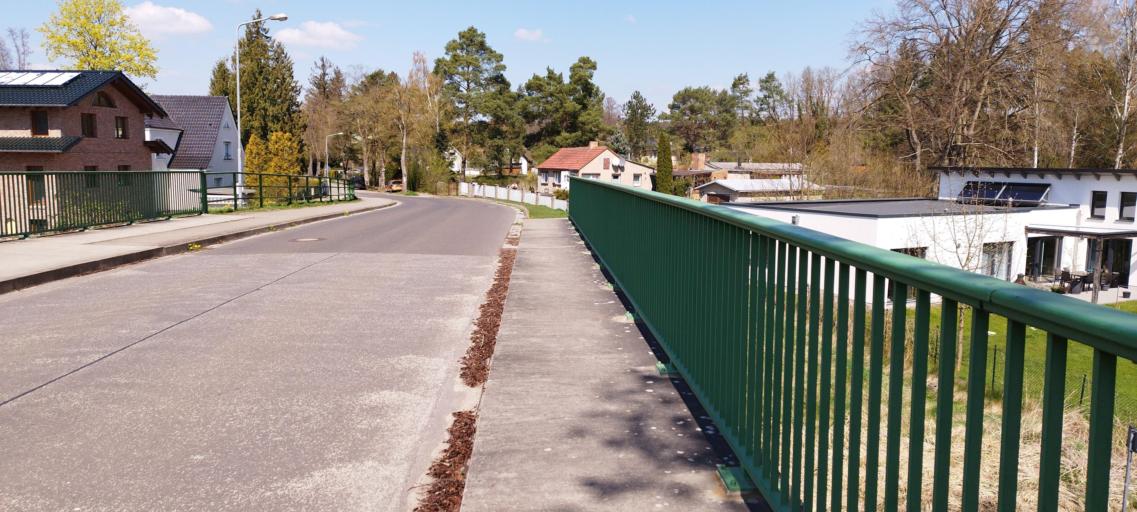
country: DE
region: Brandenburg
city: Grunheide
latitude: 52.4310
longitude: 13.8418
